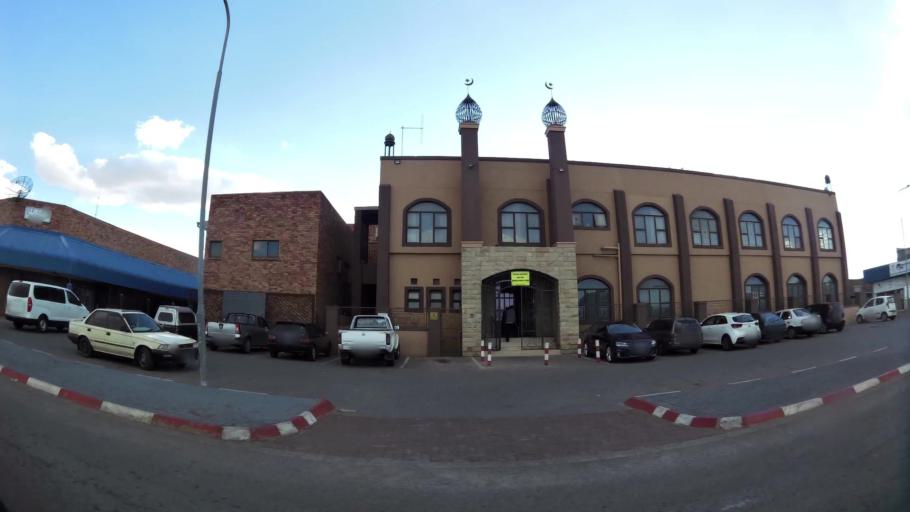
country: ZA
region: North-West
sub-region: Dr Kenneth Kaunda District Municipality
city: Potchefstroom
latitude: -26.7138
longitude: 27.0960
